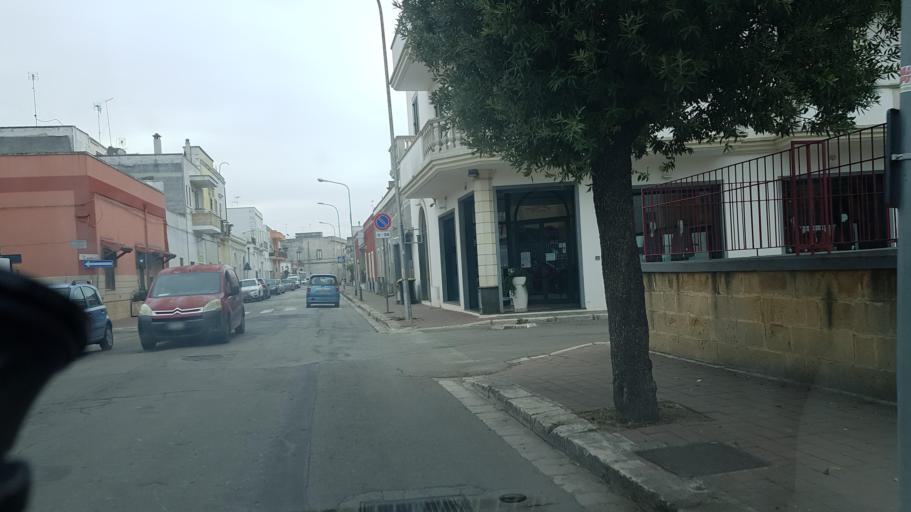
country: IT
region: Apulia
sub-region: Provincia di Lecce
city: Leverano
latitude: 40.2927
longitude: 17.9979
